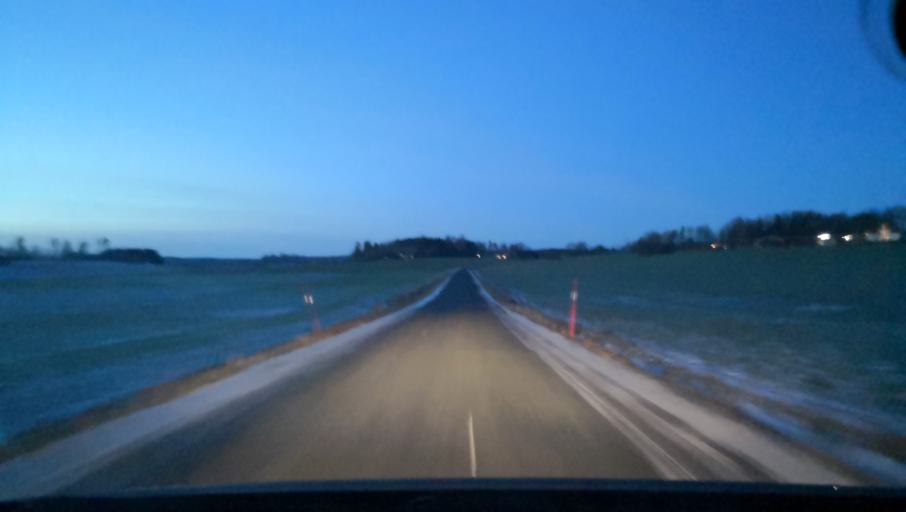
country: SE
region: Soedermanland
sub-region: Katrineholms Kommun
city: Katrineholm
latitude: 59.0763
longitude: 16.3446
